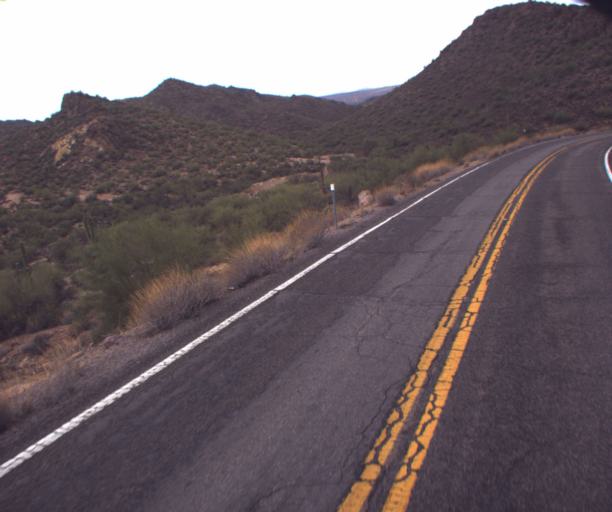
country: US
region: Arizona
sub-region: Pinal County
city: Apache Junction
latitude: 33.5430
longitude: -111.4498
